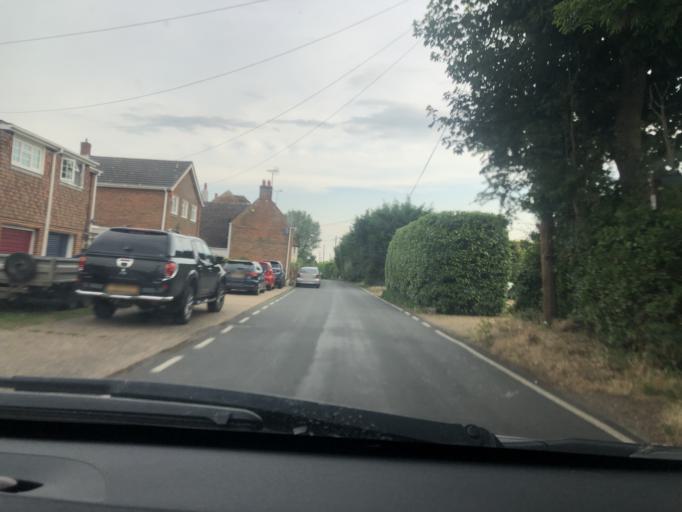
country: GB
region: England
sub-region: Kent
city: Herne Bay
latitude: 51.3398
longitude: 1.1590
